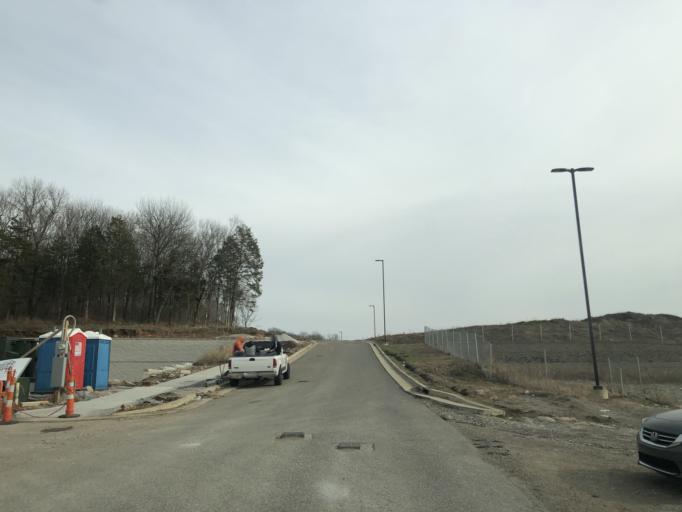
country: US
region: Tennessee
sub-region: Williamson County
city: Franklin
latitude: 35.9258
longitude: -86.8151
